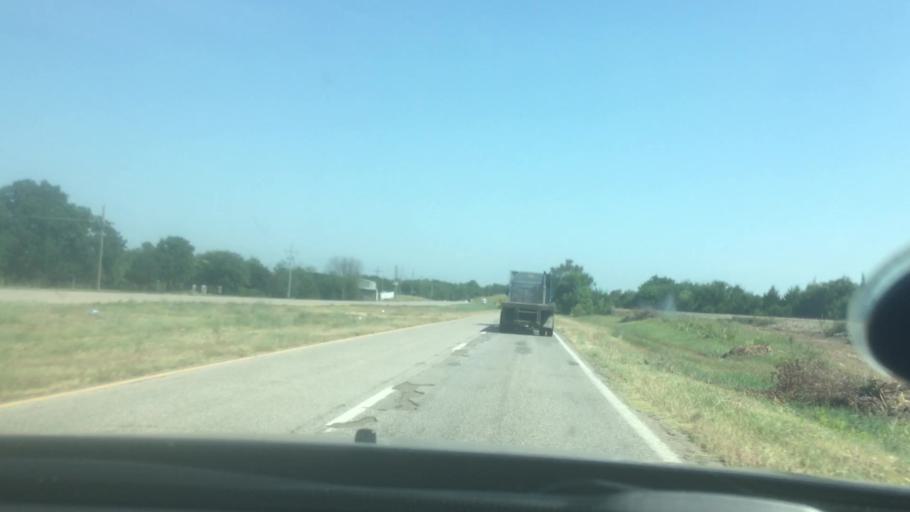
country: US
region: Oklahoma
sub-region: Pontotoc County
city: Ada
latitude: 34.7337
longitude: -96.7087
